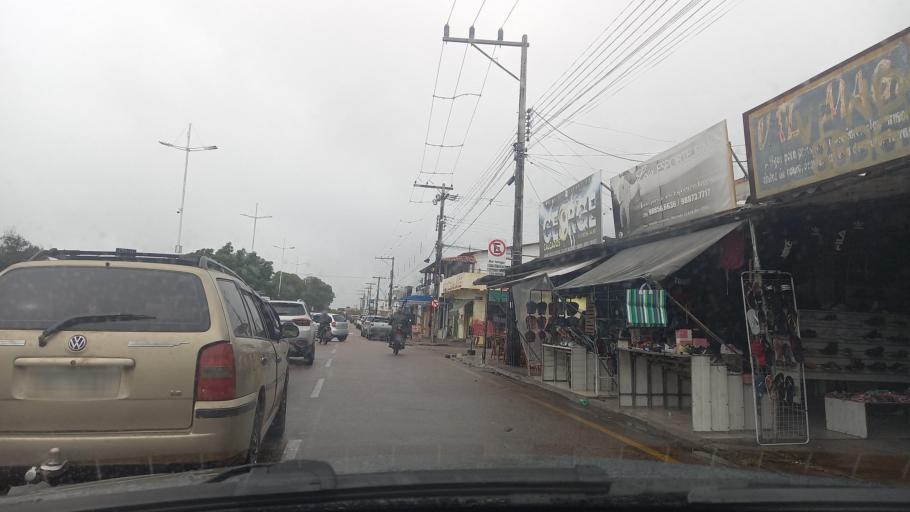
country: BR
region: Bahia
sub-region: Paulo Afonso
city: Paulo Afonso
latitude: -9.4035
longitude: -38.2277
